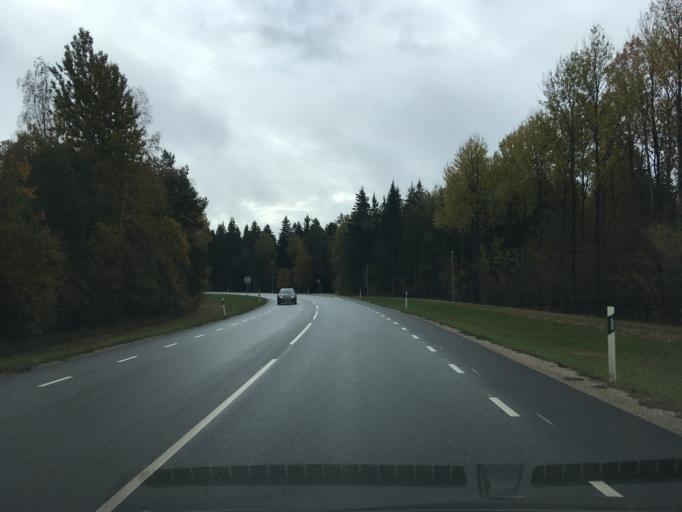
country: EE
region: Harju
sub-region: Saku vald
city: Saku
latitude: 59.3035
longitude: 24.6375
